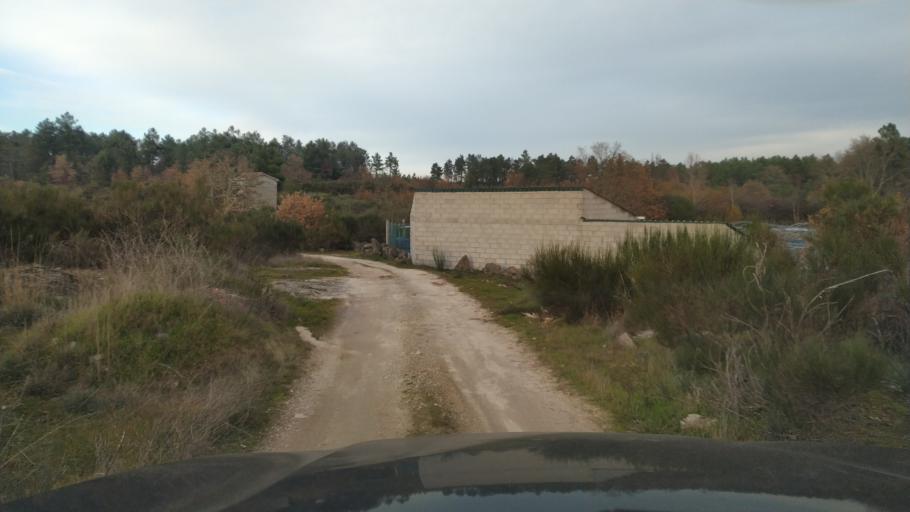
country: PT
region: Vila Real
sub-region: Sabrosa
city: Sabrosa
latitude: 41.3221
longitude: -7.6252
